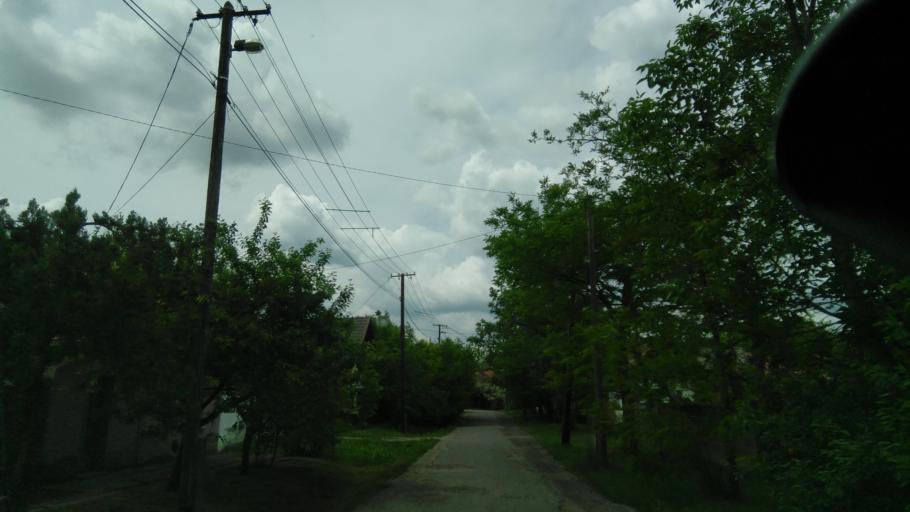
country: HU
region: Bekes
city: Totkomlos
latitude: 46.4150
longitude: 20.7273
